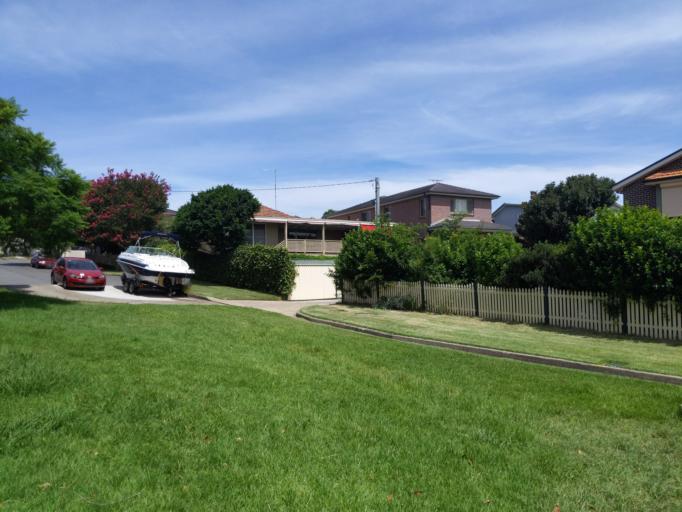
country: AU
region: New South Wales
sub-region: Canada Bay
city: Concord
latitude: -33.8435
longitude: 151.1037
